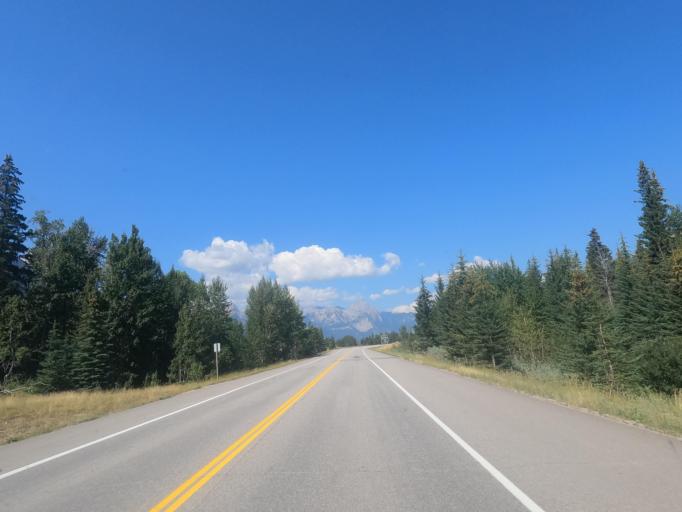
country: CA
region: Alberta
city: Jasper Park Lodge
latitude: 52.9674
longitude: -118.0549
